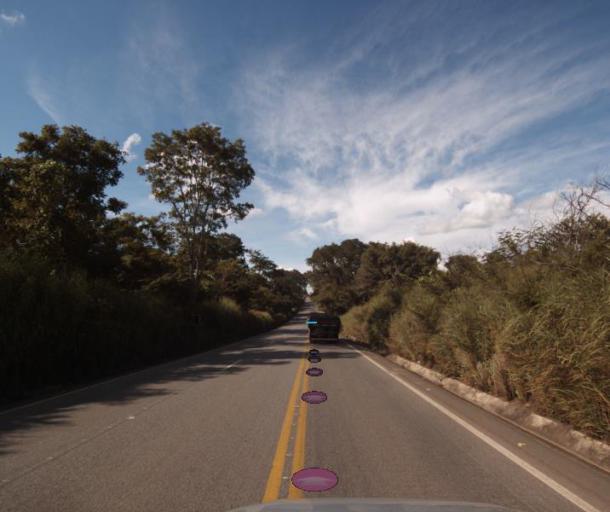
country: BR
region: Goias
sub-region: Porangatu
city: Porangatu
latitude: -13.0723
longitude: -49.1863
